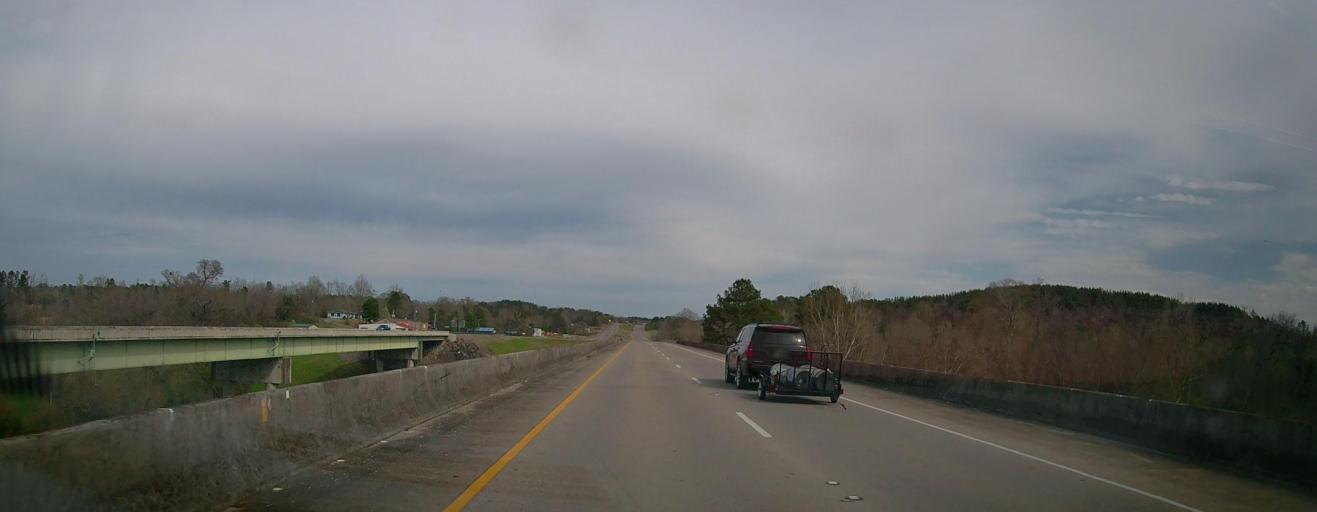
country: US
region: Alabama
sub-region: Walker County
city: Cordova
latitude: 33.8067
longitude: -87.1411
